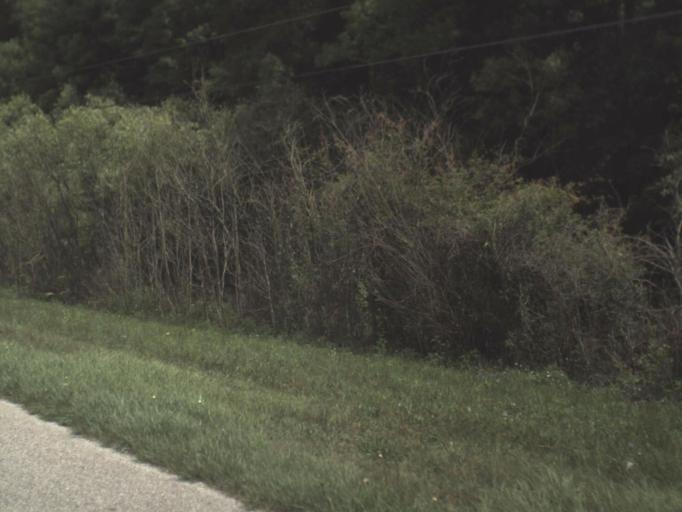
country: US
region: Florida
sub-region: Saint Johns County
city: Palm Valley
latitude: 30.0540
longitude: -81.4293
